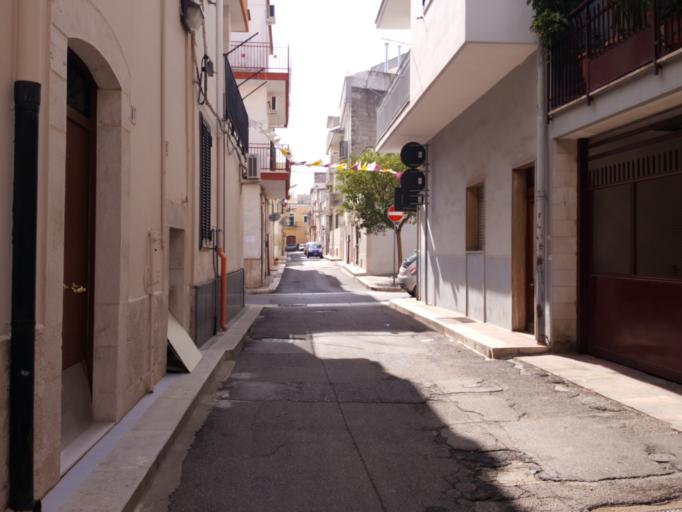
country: IT
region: Apulia
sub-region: Provincia di Bari
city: Triggiano
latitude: 41.0640
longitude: 16.9253
